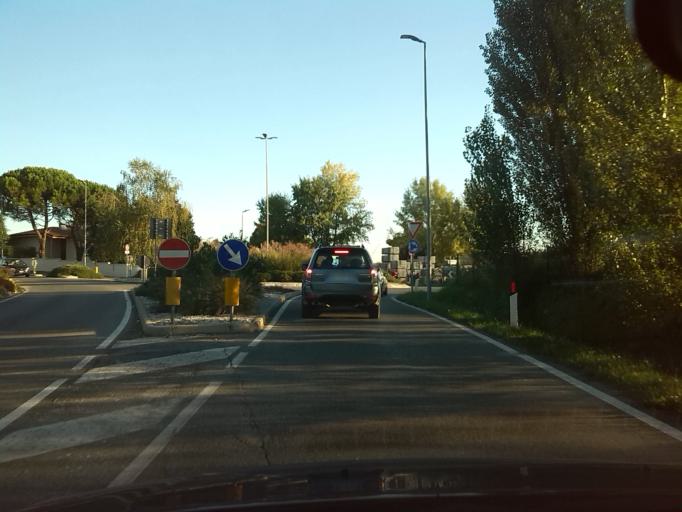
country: IT
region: Friuli Venezia Giulia
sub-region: Provincia di Udine
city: Colugna
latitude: 46.0891
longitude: 13.1962
